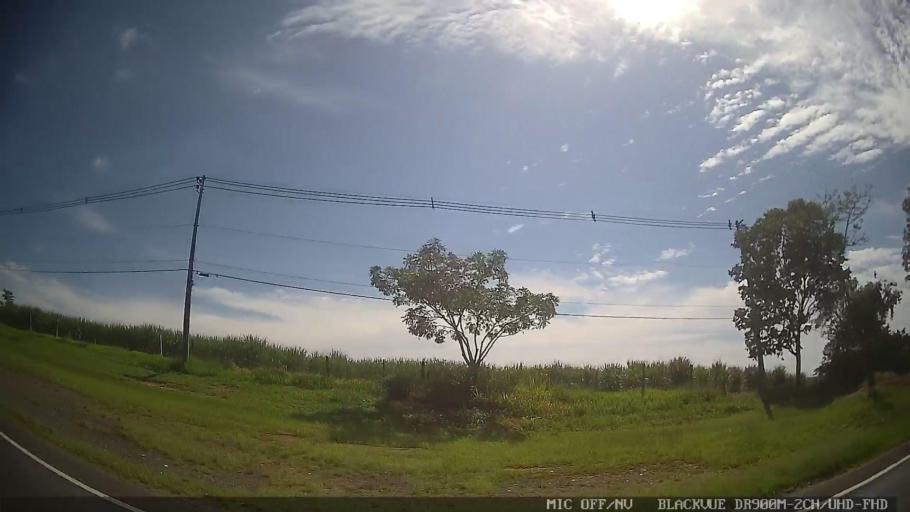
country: BR
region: Sao Paulo
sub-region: Porto Feliz
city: Porto Feliz
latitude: -23.2149
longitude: -47.5734
